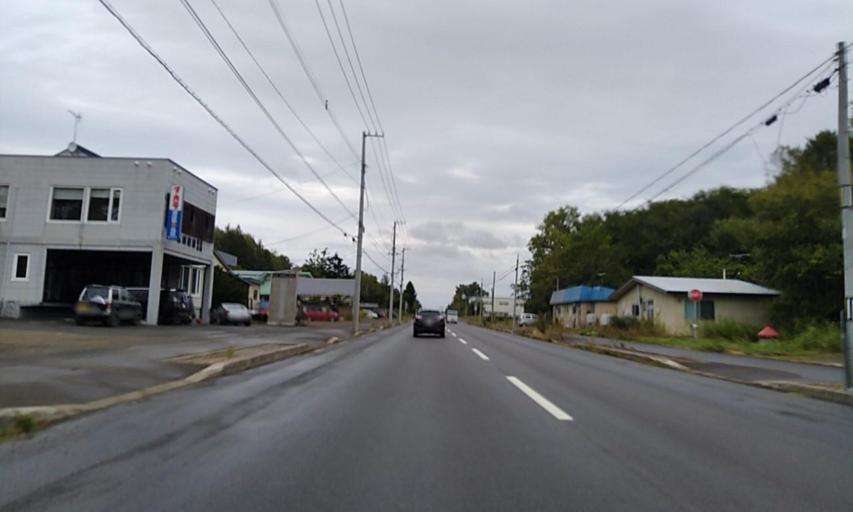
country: JP
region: Hokkaido
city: Kitami
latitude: 44.0822
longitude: 143.9457
